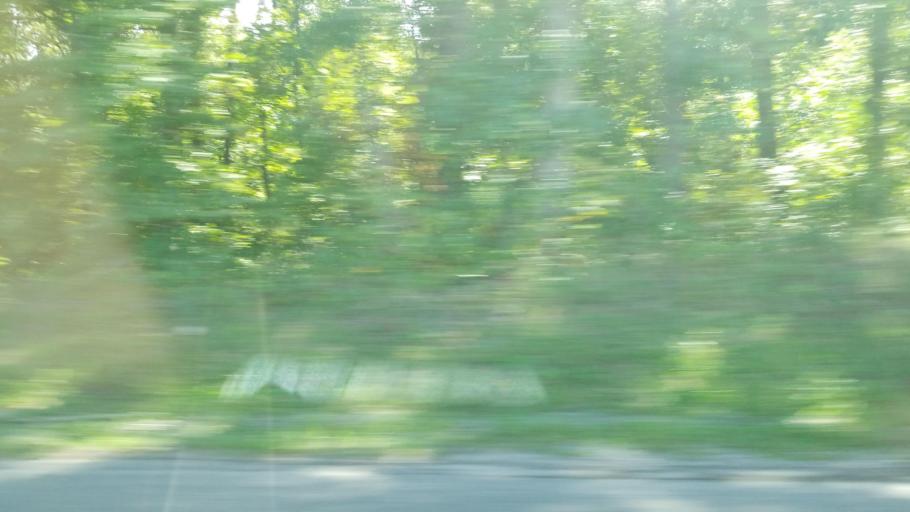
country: US
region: Illinois
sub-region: Williamson County
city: Johnston City
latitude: 37.7903
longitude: -88.8288
